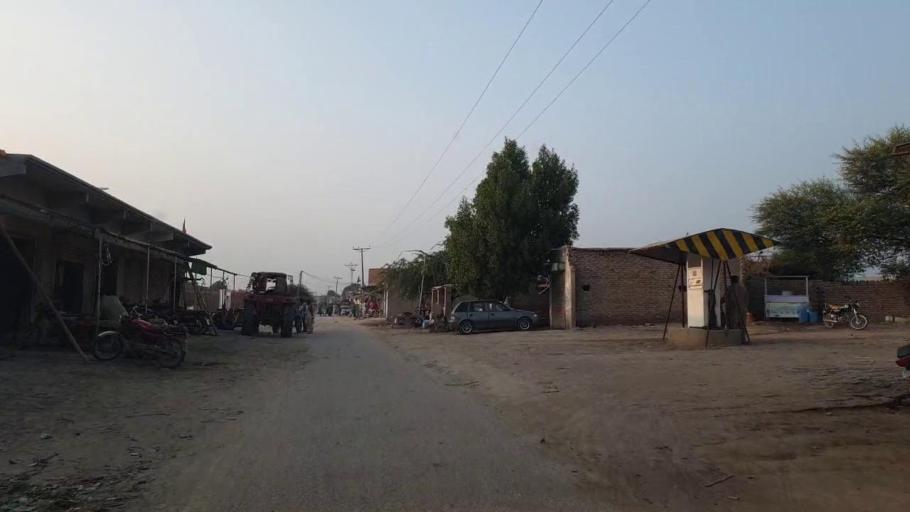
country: PK
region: Sindh
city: Tando Ghulam Ali
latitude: 25.1445
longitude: 68.9571
